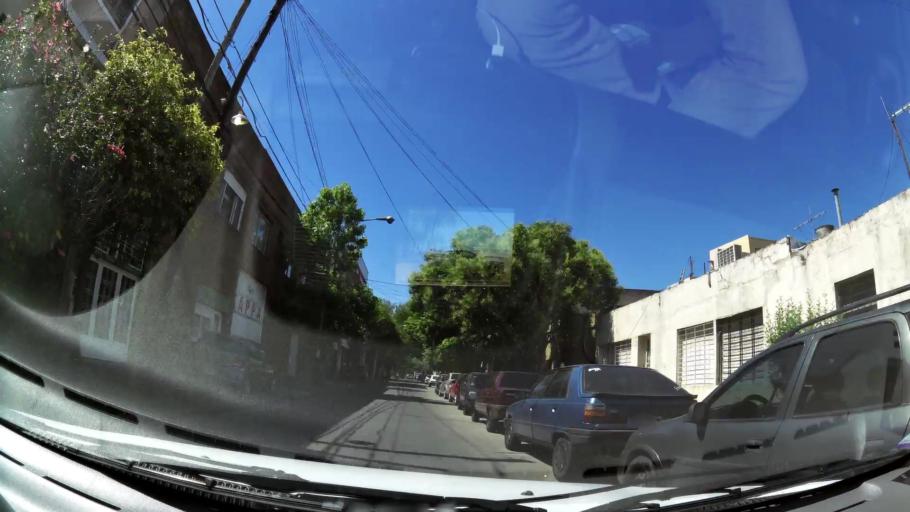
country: AR
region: Buenos Aires
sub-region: Partido de General San Martin
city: General San Martin
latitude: -34.5843
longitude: -58.5264
